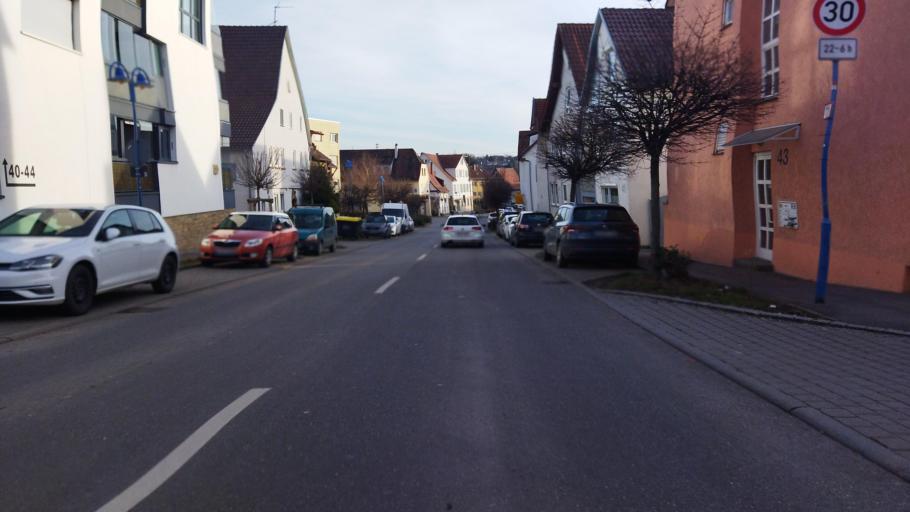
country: DE
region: Baden-Wuerttemberg
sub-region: Regierungsbezirk Stuttgart
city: Asperg
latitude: 48.9078
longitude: 9.1350
